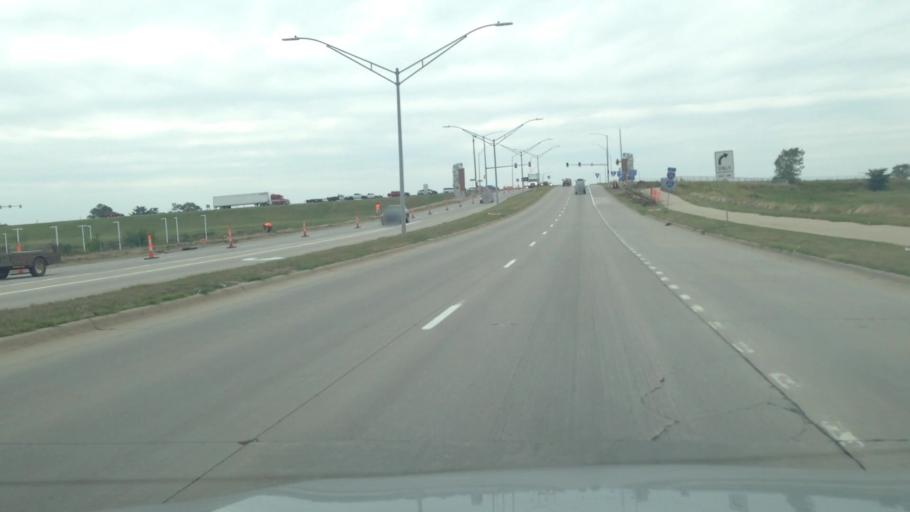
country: US
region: Iowa
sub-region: Polk County
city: Clive
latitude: 41.6295
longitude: -93.7718
